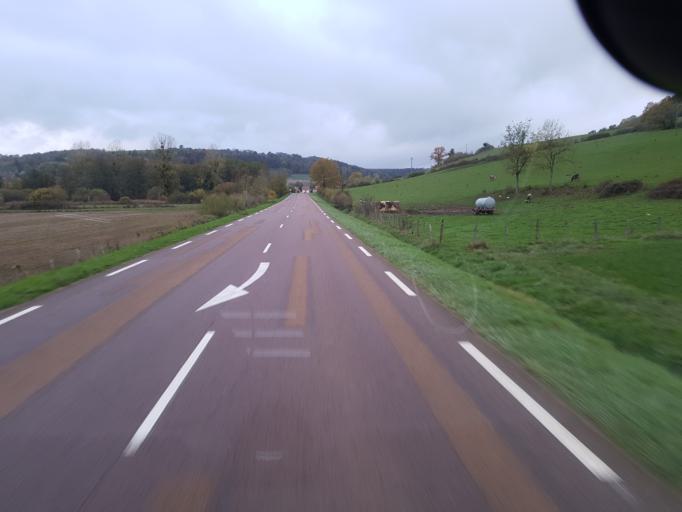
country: FR
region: Bourgogne
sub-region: Departement de la Cote-d'Or
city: Chatillon-sur-Seine
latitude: 47.6766
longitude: 4.6777
